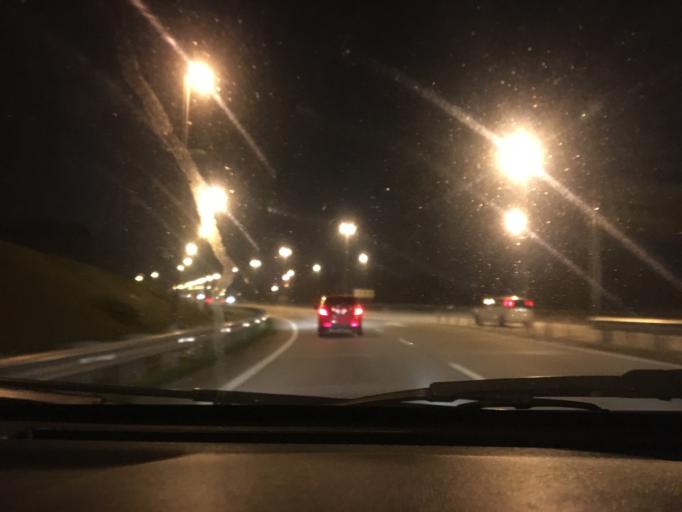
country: MY
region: Selangor
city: Kampong Baharu Balakong
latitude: 2.9832
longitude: 101.7316
